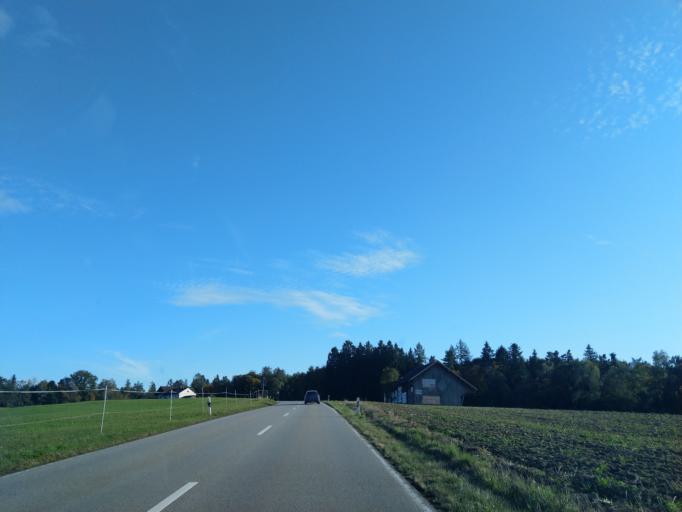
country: DE
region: Bavaria
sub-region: Lower Bavaria
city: Deggendorf
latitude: 48.8557
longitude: 12.9427
